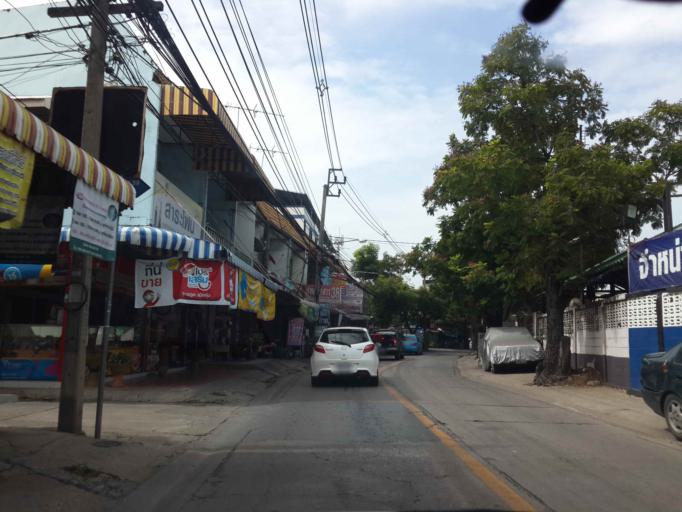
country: TH
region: Bangkok
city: Bang Khen
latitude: 13.8601
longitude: 100.6278
